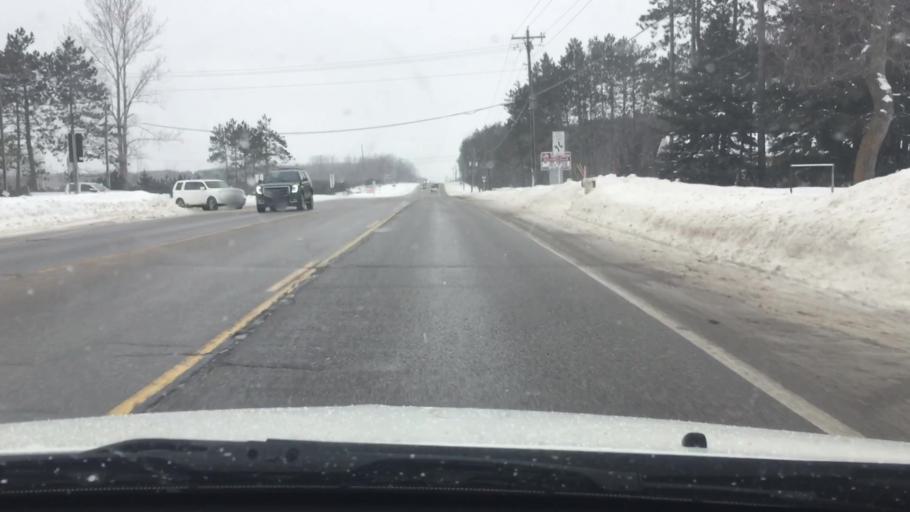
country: US
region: Michigan
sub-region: Otsego County
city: Gaylord
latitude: 45.0276
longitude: -84.7263
